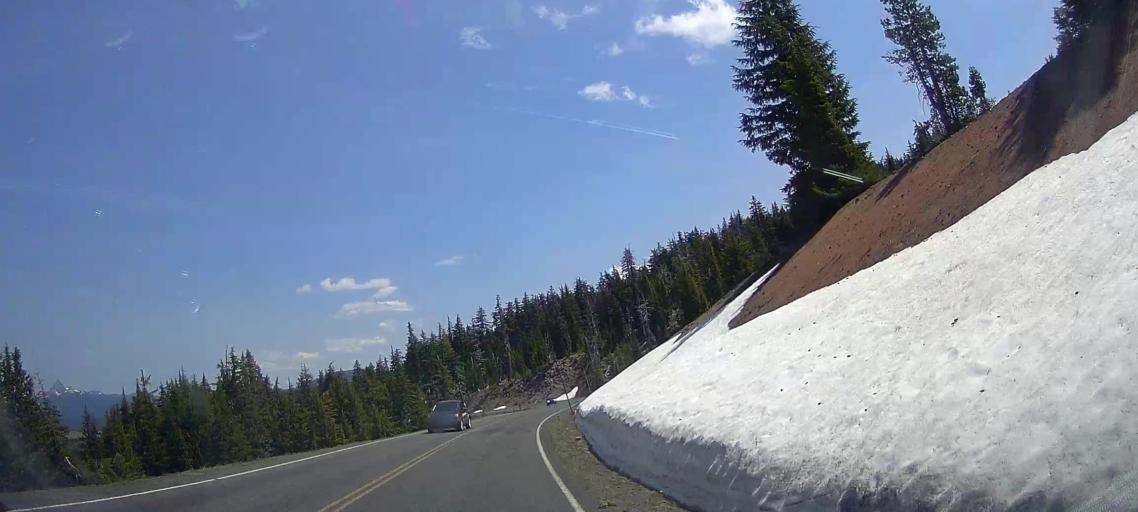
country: US
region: Oregon
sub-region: Jackson County
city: Shady Cove
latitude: 42.9852
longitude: -122.1481
